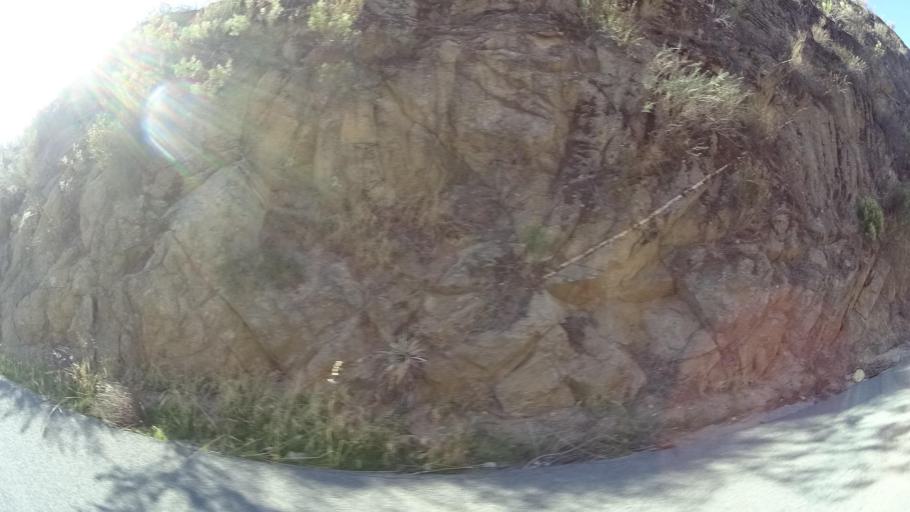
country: MX
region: Baja California
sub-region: Tecate
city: Lomas de Santa Anita
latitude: 32.6106
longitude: -116.6998
